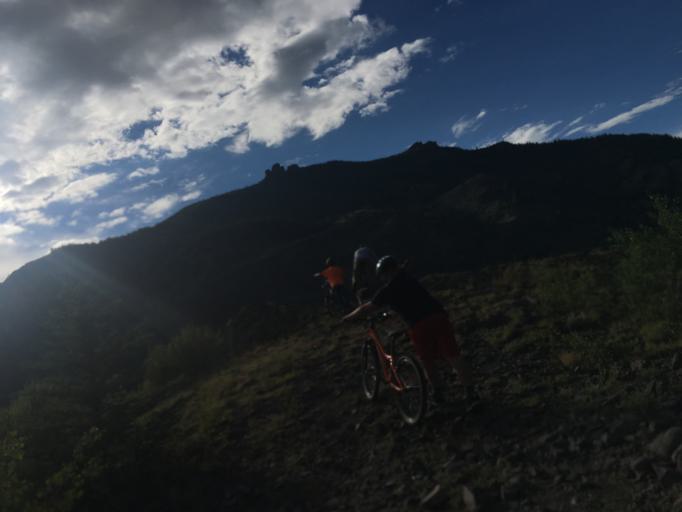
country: US
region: Colorado
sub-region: Hinsdale County
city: Lake City
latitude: 37.9575
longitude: -107.2941
